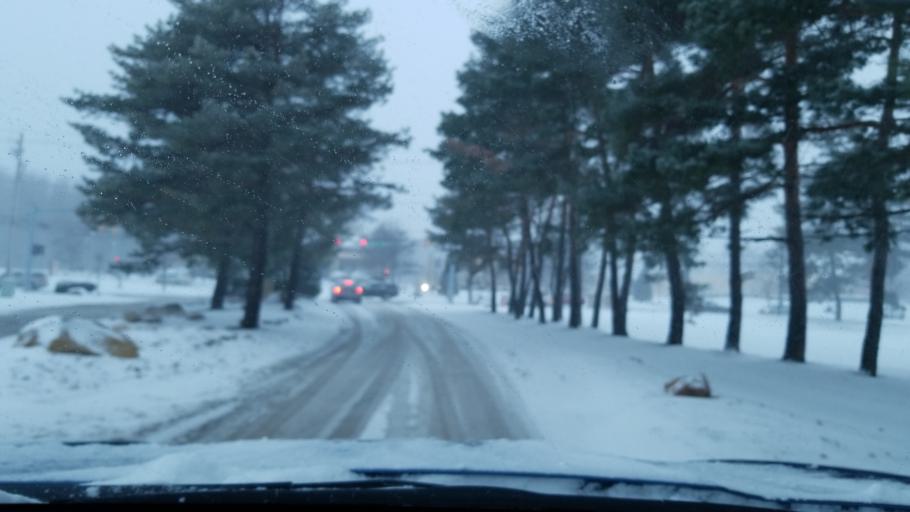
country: US
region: Ohio
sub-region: Cuyahoga County
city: Strongsville
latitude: 41.3238
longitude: -81.8358
